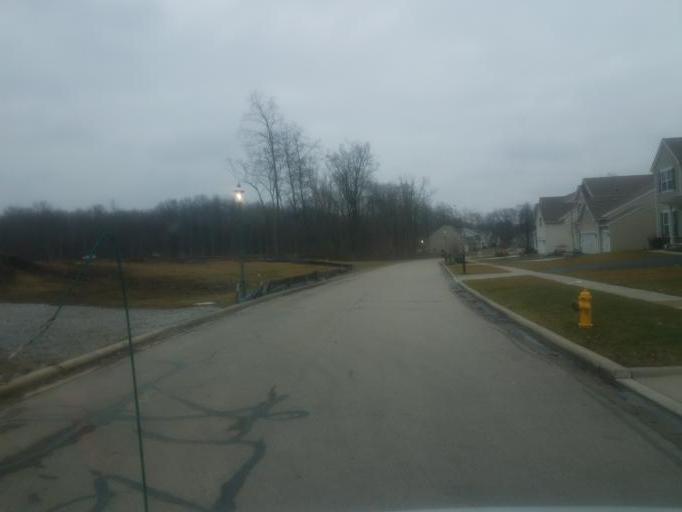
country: US
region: Ohio
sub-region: Delaware County
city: Sunbury
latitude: 40.2184
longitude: -82.8921
